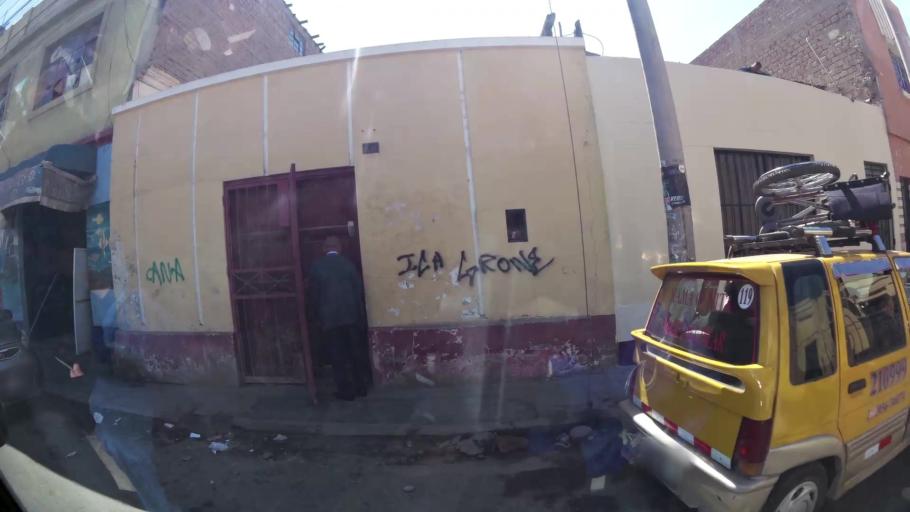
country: PE
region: Ica
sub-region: Provincia de Ica
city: Ica
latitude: -14.0660
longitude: -75.7262
